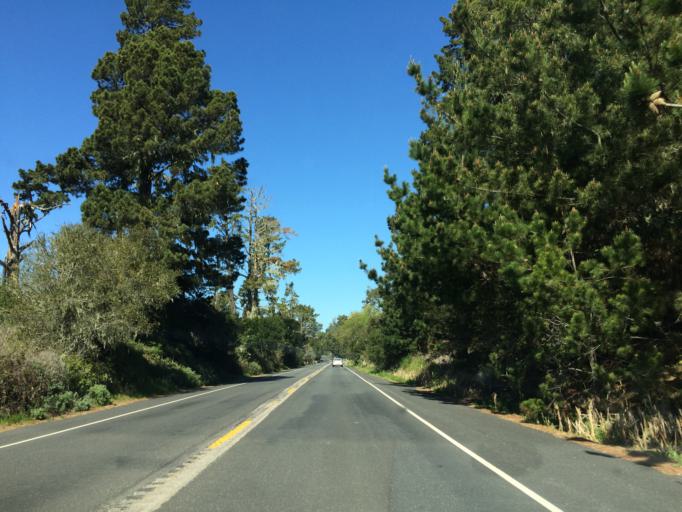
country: US
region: California
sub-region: Santa Cruz County
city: Bonny Doon
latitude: 37.1178
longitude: -122.3042
